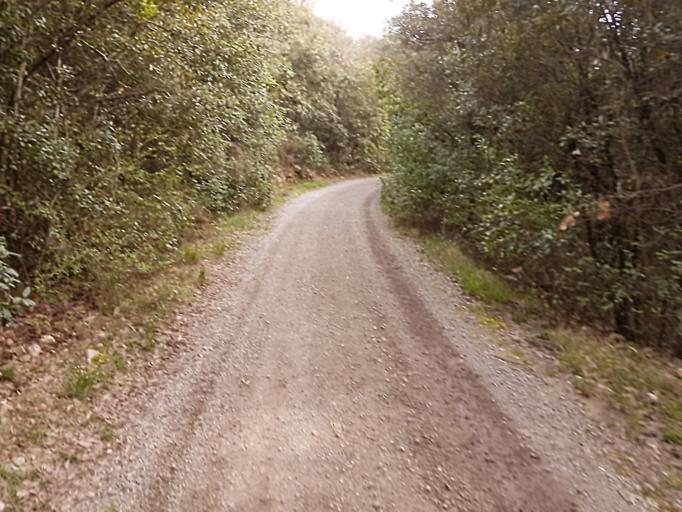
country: IT
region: Umbria
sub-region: Provincia di Perugia
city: Corciano
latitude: 43.1333
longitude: 12.2993
